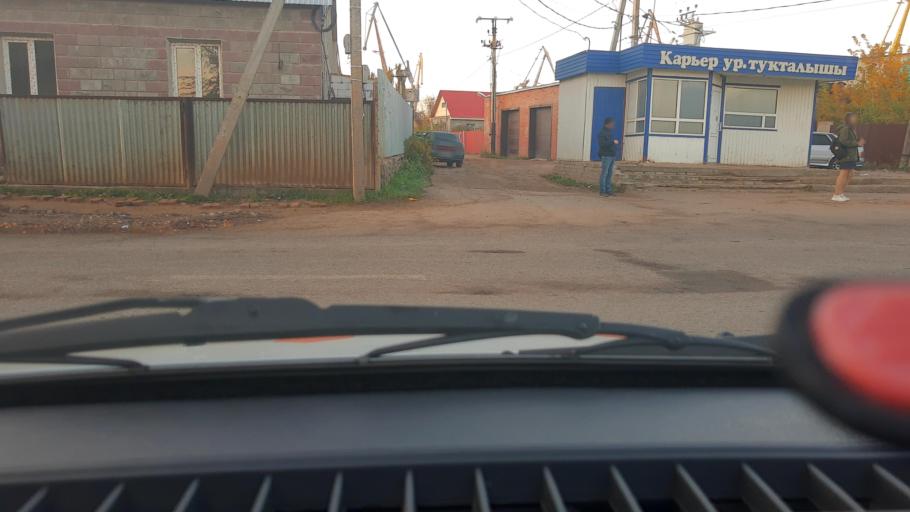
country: RU
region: Bashkortostan
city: Ufa
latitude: 54.7290
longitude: 55.9001
